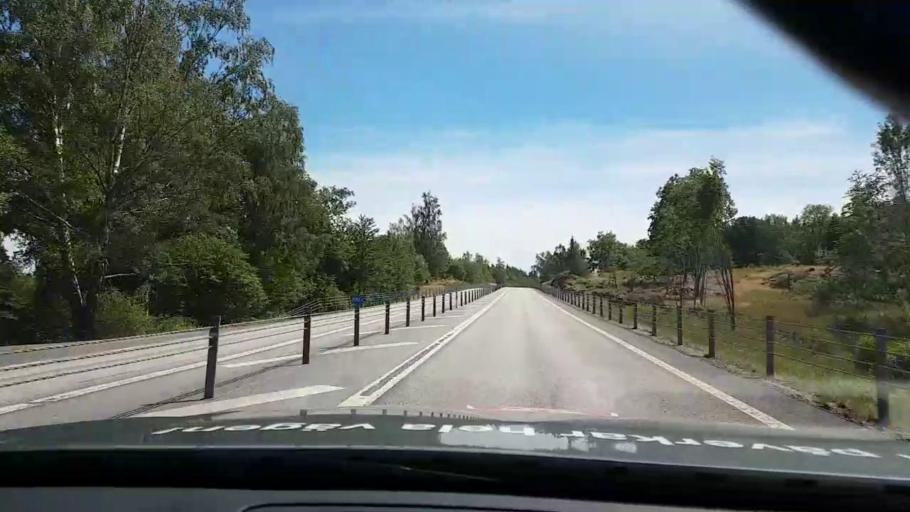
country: SE
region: Kalmar
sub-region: Vasterviks Kommun
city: Gamleby
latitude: 57.8651
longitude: 16.4204
